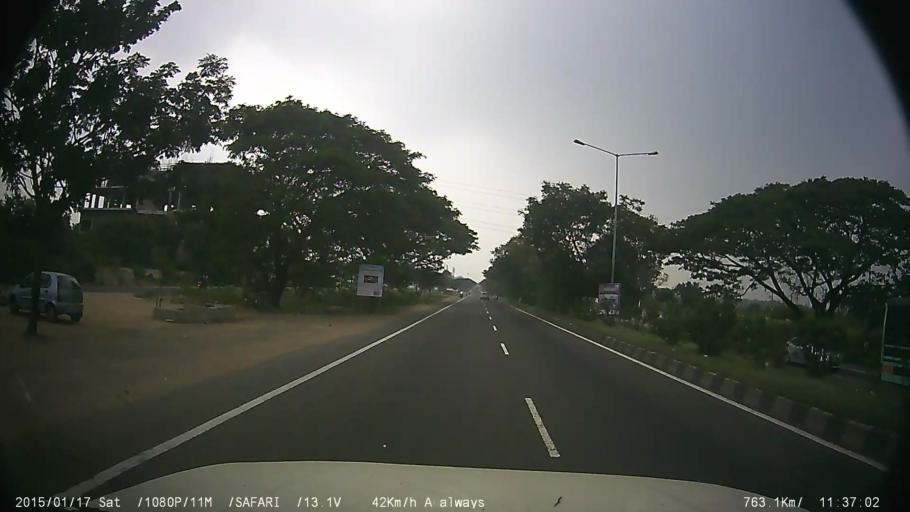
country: IN
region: Tamil Nadu
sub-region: Kancheepuram
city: Singapperumalkovil
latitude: 12.8054
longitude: 80.0271
